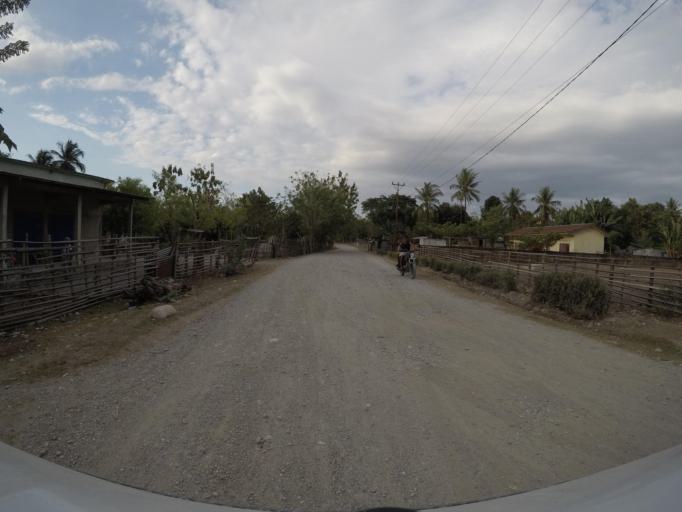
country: TL
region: Bobonaro
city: Maliana
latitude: -8.8800
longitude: 125.2114
